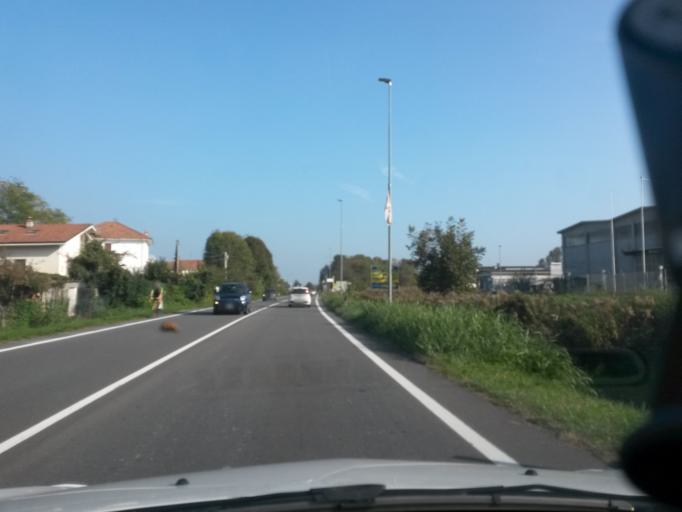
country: IT
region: Piedmont
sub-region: Provincia di Torino
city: Villar Dora
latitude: 45.1017
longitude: 7.3882
